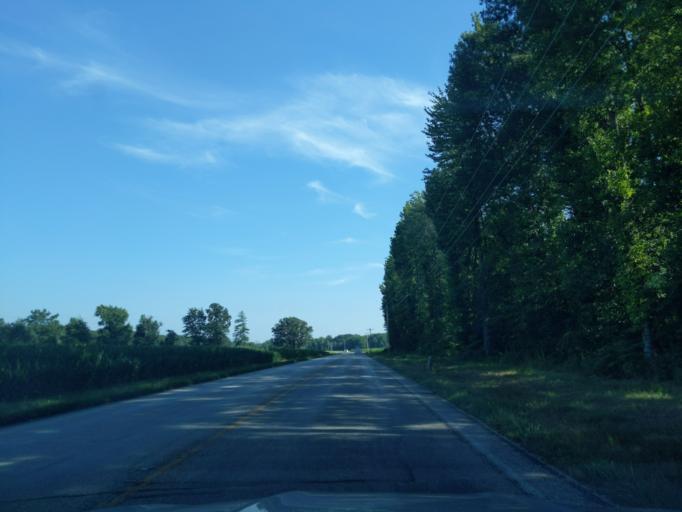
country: US
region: Indiana
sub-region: Ripley County
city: Versailles
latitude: 39.0946
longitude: -85.2767
